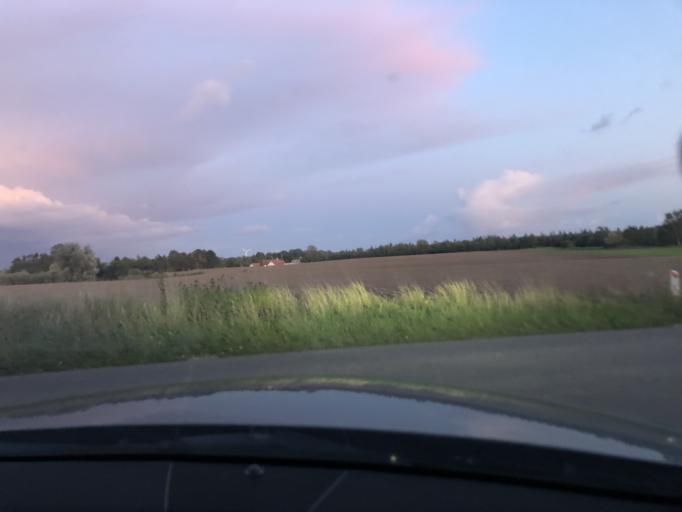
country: DK
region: Zealand
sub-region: Soro Kommune
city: Stenlille
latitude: 55.6559
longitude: 11.6118
